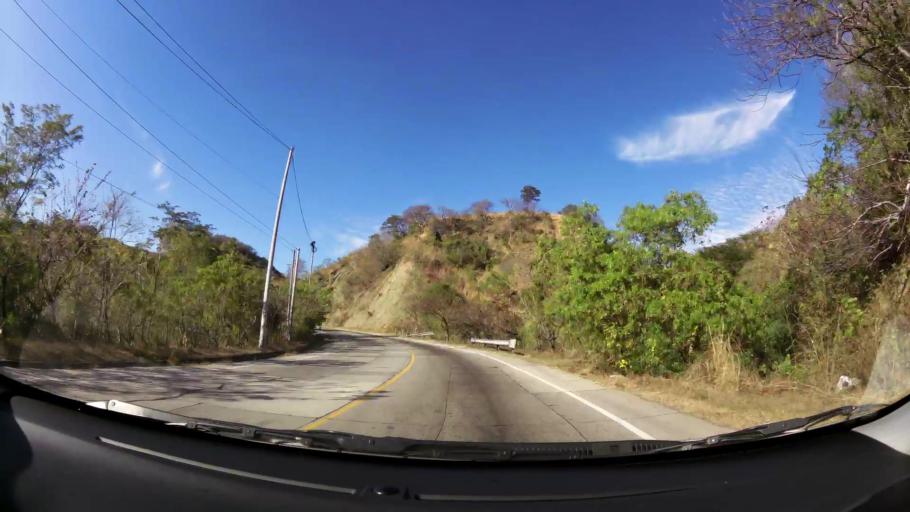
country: SV
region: Santa Ana
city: Texistepeque
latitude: 14.1462
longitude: -89.5140
